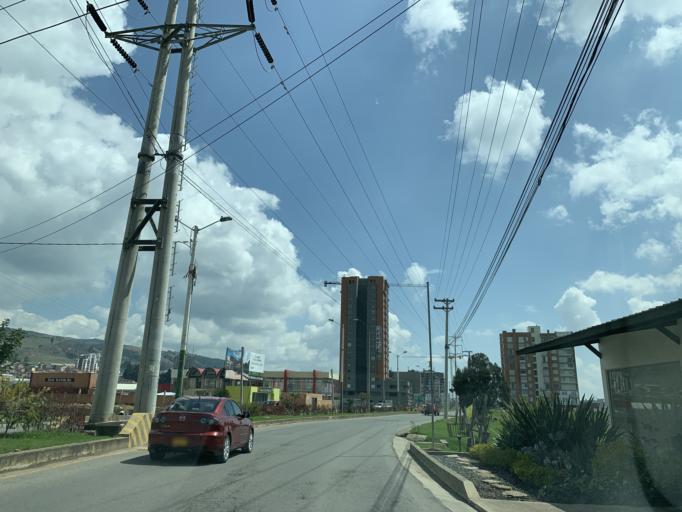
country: CO
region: Boyaca
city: Tunja
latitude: 5.5577
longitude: -73.3446
